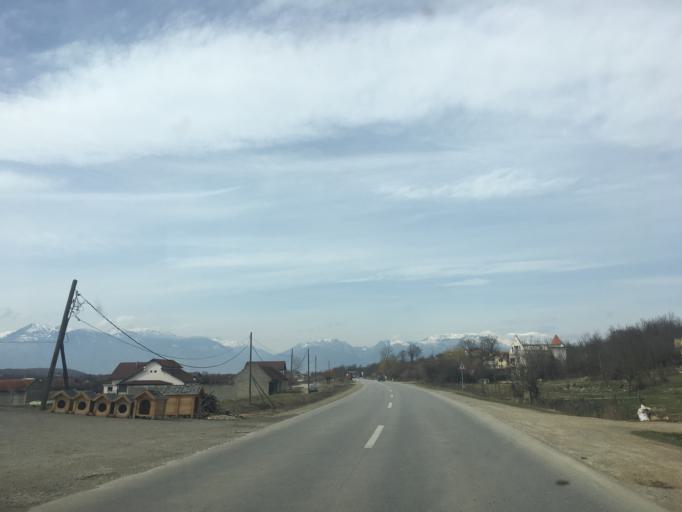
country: XK
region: Pec
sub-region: Komuna e Pejes
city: Kosuriq
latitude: 42.6157
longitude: 20.4970
